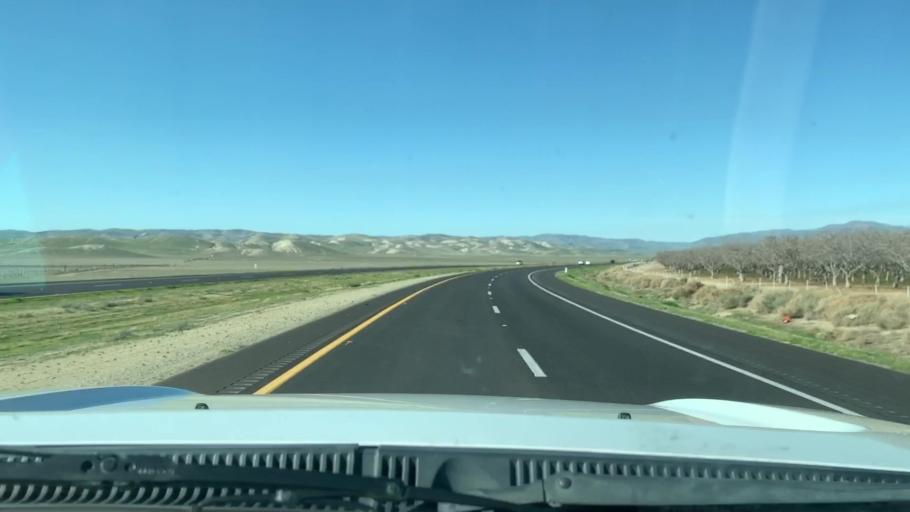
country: US
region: California
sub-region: Kern County
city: Lost Hills
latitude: 35.6147
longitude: -119.9644
